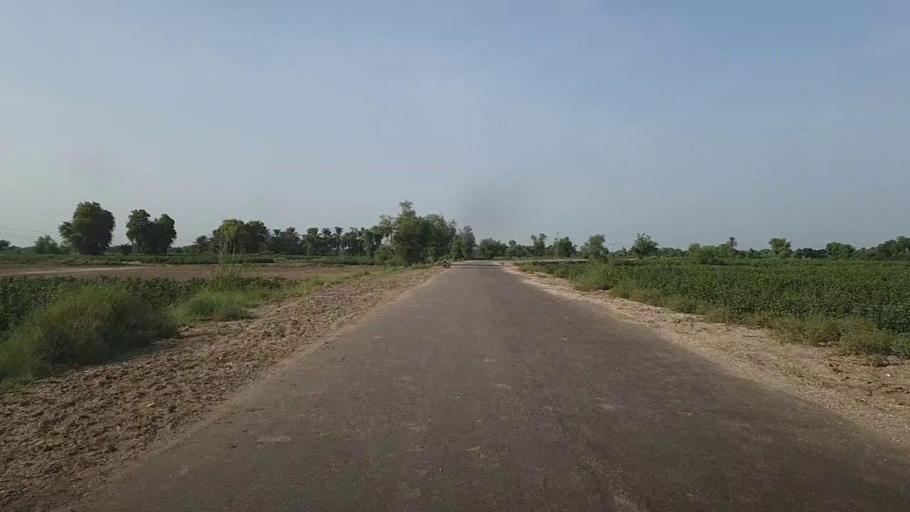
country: PK
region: Sindh
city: Ubauro
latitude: 28.1061
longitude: 69.8475
